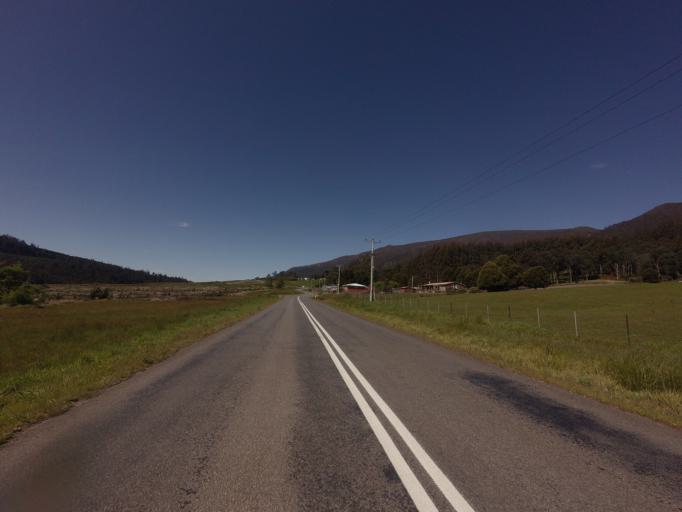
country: AU
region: Tasmania
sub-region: Derwent Valley
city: New Norfolk
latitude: -42.7537
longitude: 146.6317
